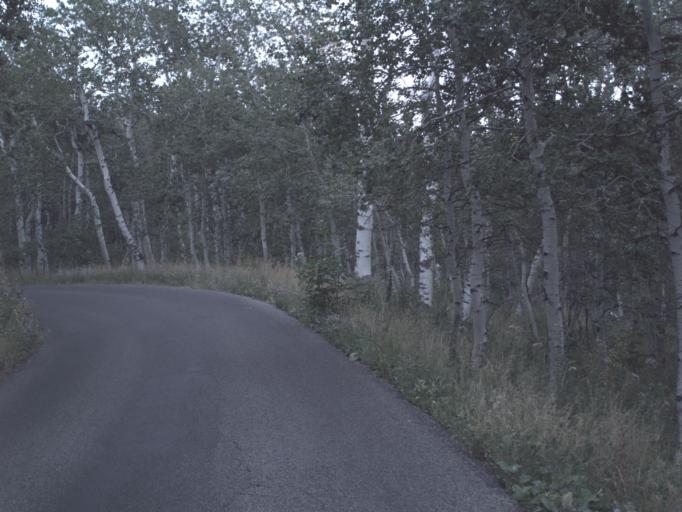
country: US
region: Utah
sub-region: Utah County
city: Lindon
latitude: 40.4202
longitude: -111.6059
